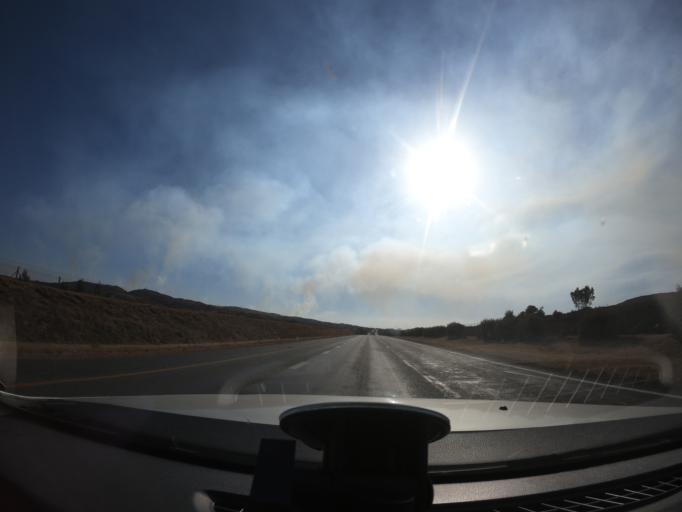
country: ZA
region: Gauteng
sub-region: Sedibeng District Municipality
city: Heidelberg
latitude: -26.4877
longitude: 28.3681
